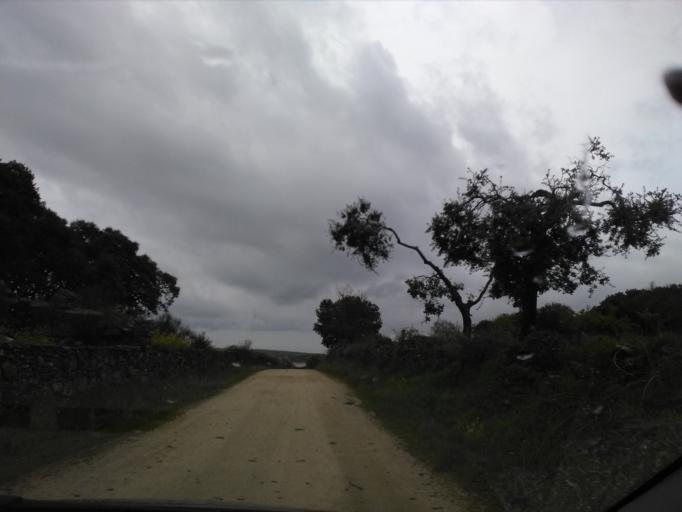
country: ES
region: Castille and Leon
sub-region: Provincia de Salamanca
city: San Felices de los Gallegos
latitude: 40.8394
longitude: -6.7282
